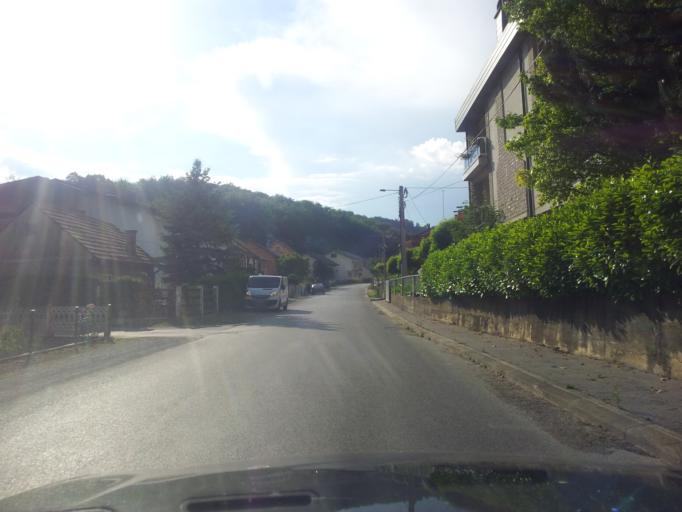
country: HR
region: Karlovacka
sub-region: Grad Karlovac
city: Karlovac
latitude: 45.4595
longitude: 15.4830
